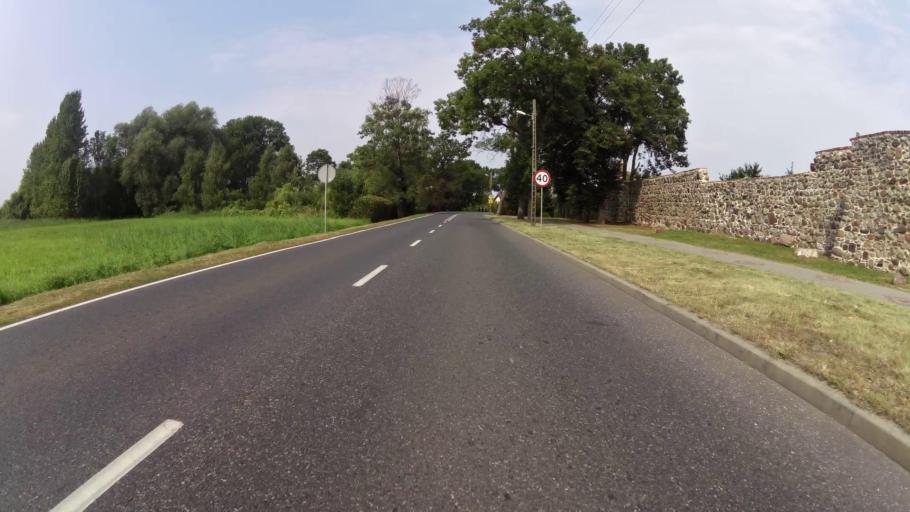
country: PL
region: West Pomeranian Voivodeship
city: Trzcinsko Zdroj
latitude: 52.9633
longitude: 14.6063
